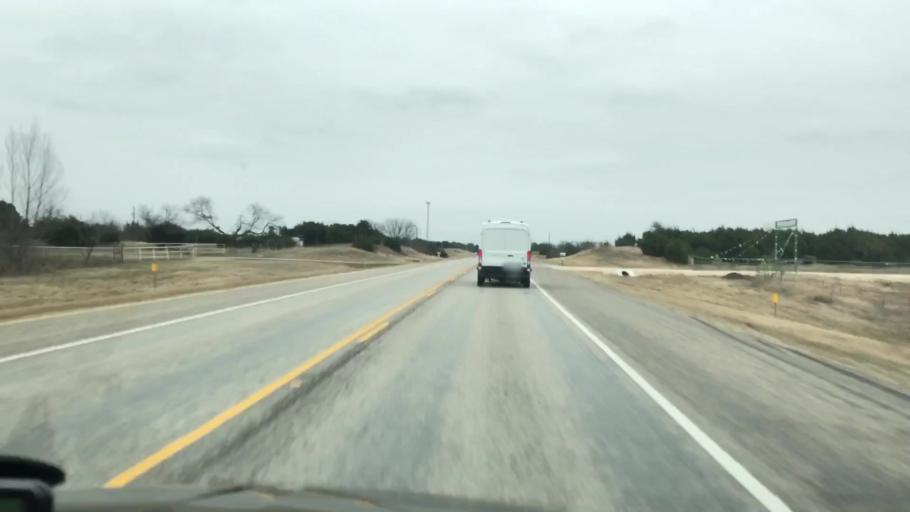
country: US
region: Texas
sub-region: Lampasas County
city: Lampasas
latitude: 31.1248
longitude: -98.1903
